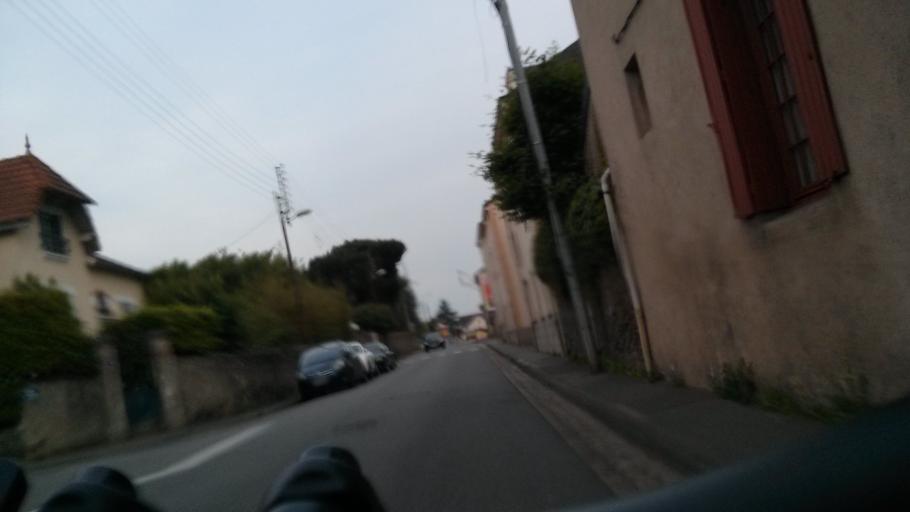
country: FR
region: Pays de la Loire
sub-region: Departement de la Loire-Atlantique
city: Reze
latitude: 47.1902
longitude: -1.5332
